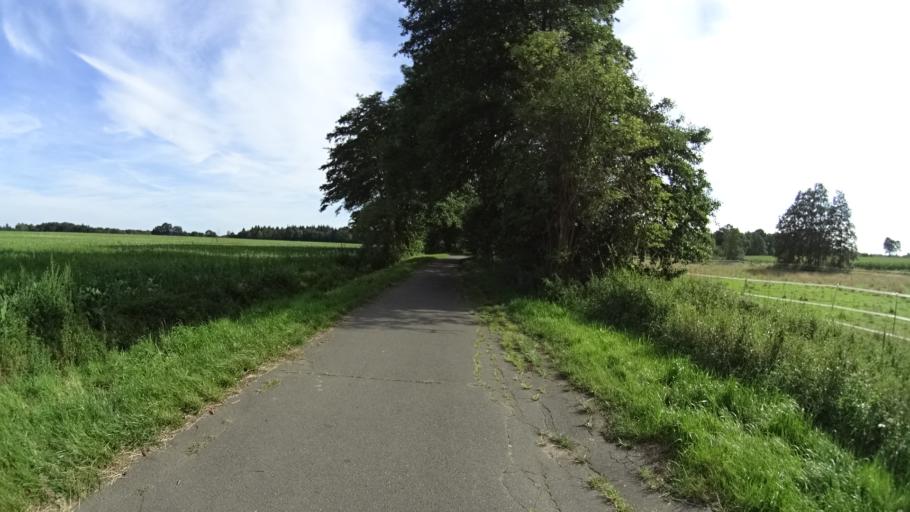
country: DE
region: Lower Saxony
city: Reppenstedt
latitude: 53.2425
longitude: 10.3602
